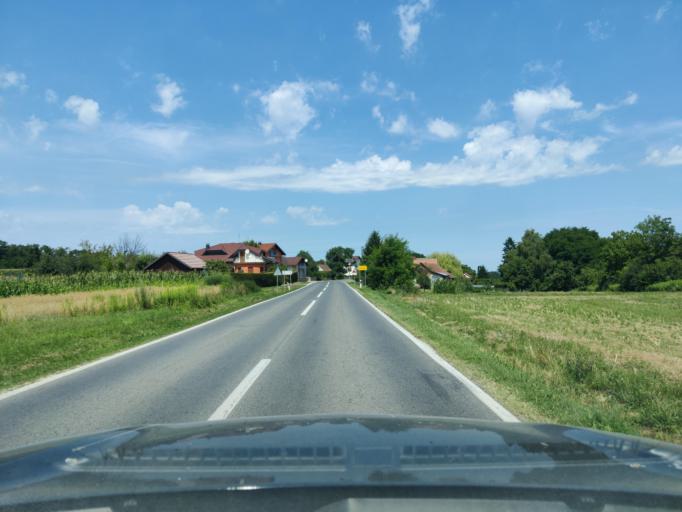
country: HR
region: Medimurska
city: Vratisinec
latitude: 46.4668
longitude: 16.4256
